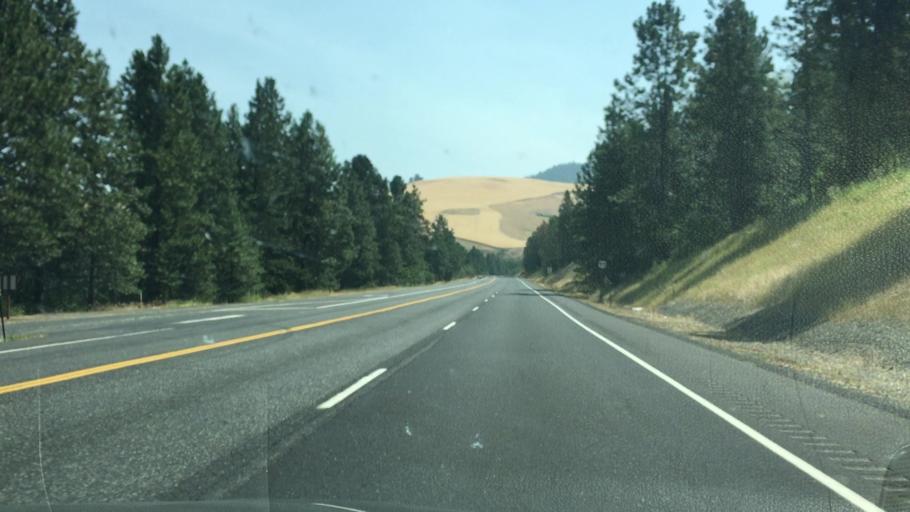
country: US
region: Idaho
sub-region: Nez Perce County
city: Lapwai
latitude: 46.3726
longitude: -116.6651
